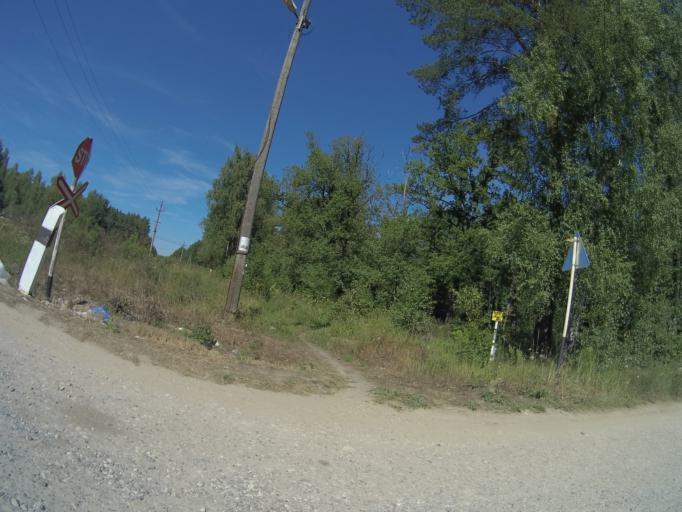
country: RU
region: Vladimir
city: Raduzhnyy
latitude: 56.0650
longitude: 40.3700
